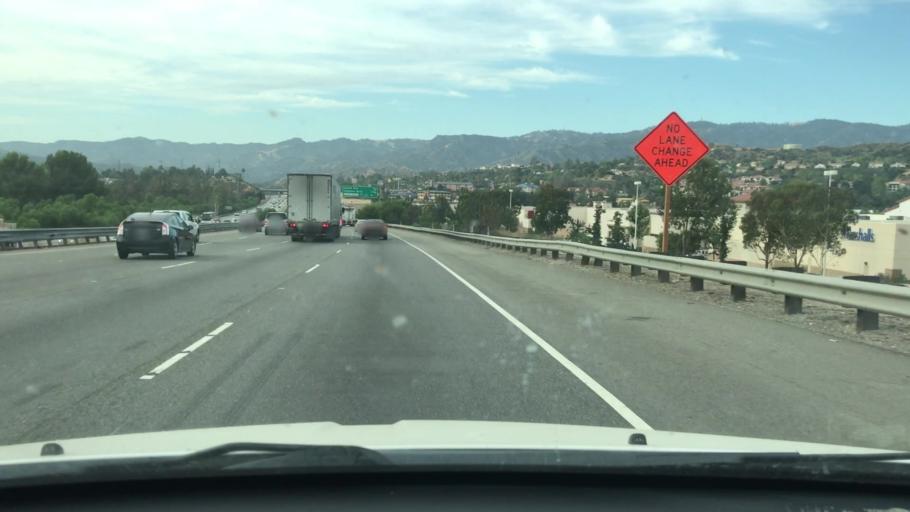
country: US
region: California
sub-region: Los Angeles County
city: Santa Clarita
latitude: 34.3889
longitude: -118.5702
